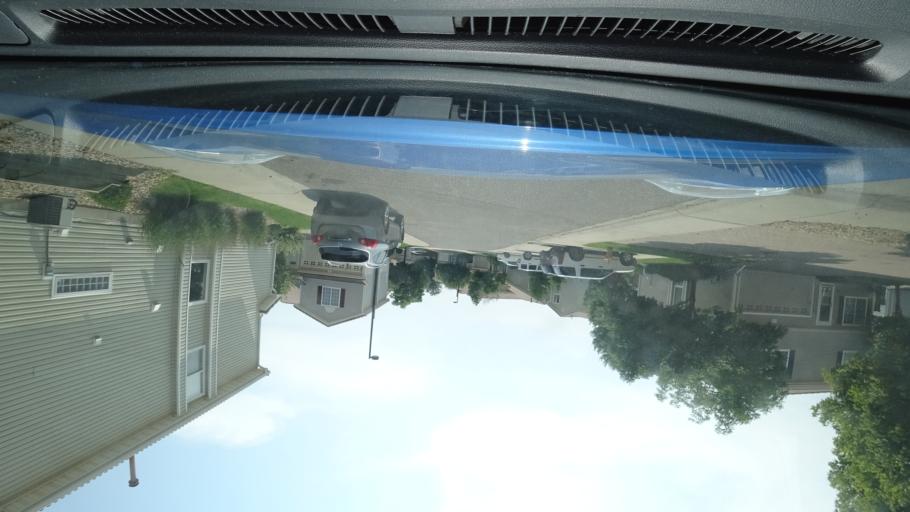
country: US
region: Colorado
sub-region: Adams County
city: Aurora
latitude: 39.7756
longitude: -104.7549
